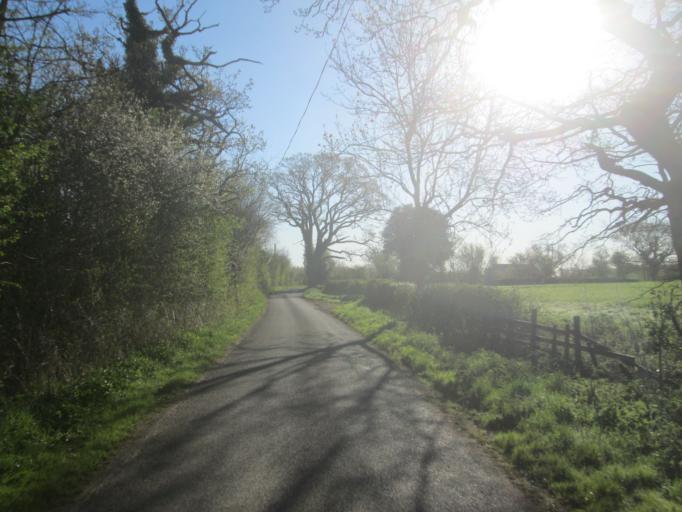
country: GB
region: England
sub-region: Derbyshire
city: Yeldersley
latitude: 52.9736
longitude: -1.5821
